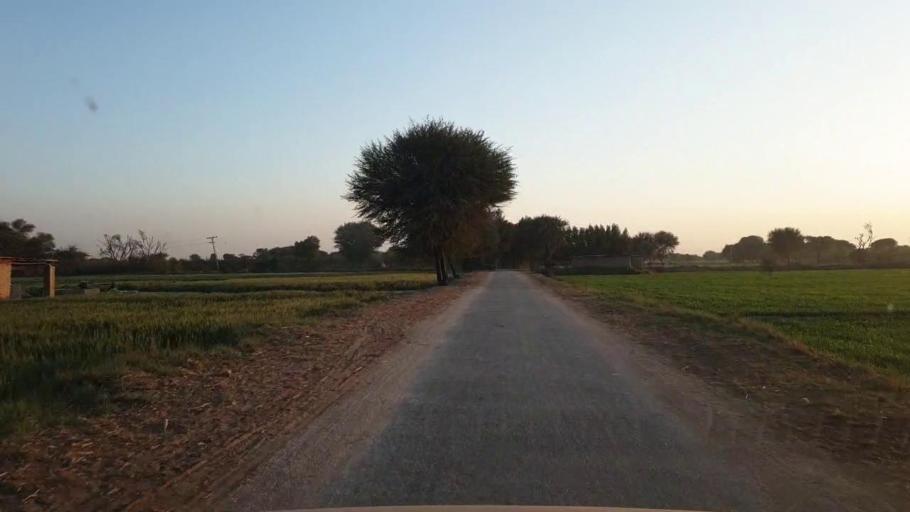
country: PK
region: Sindh
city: Tando Jam
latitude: 25.3048
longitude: 68.6379
